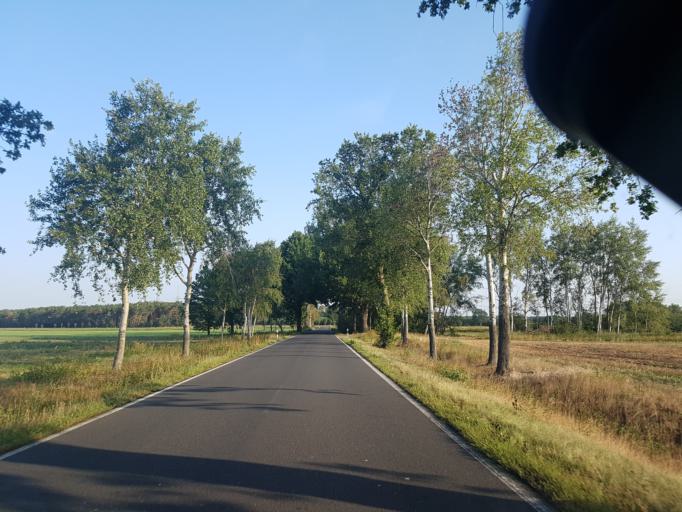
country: DE
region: Saxony-Anhalt
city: Holzdorf
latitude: 51.8240
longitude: 13.1419
